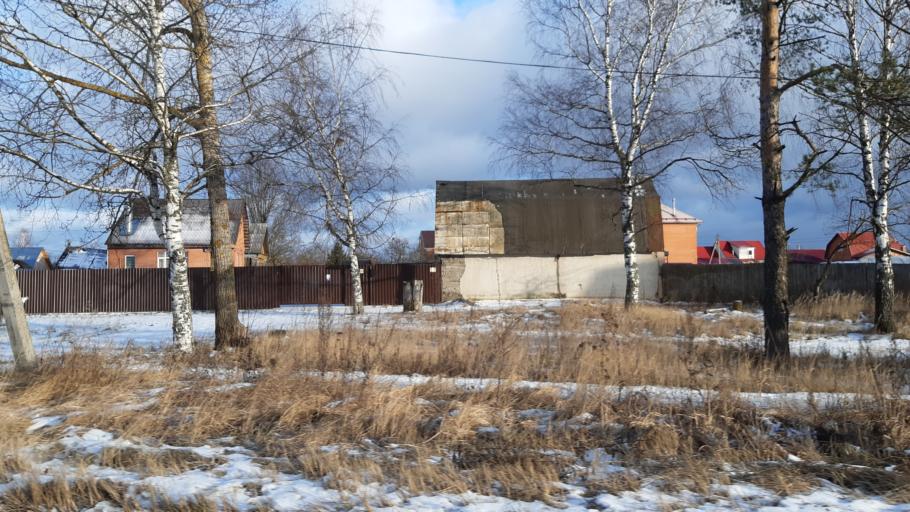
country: RU
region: Moskovskaya
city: Noginsk-9
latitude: 56.0514
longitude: 38.5510
